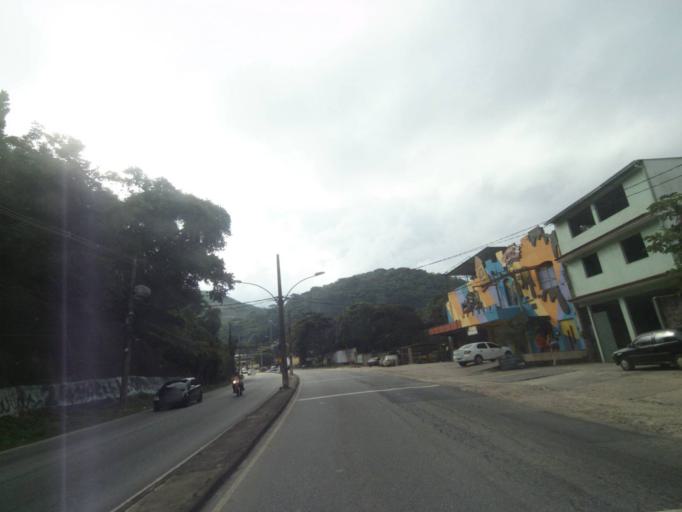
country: BR
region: Rio de Janeiro
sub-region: Sao Joao De Meriti
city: Sao Joao de Meriti
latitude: -22.9018
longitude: -43.3814
